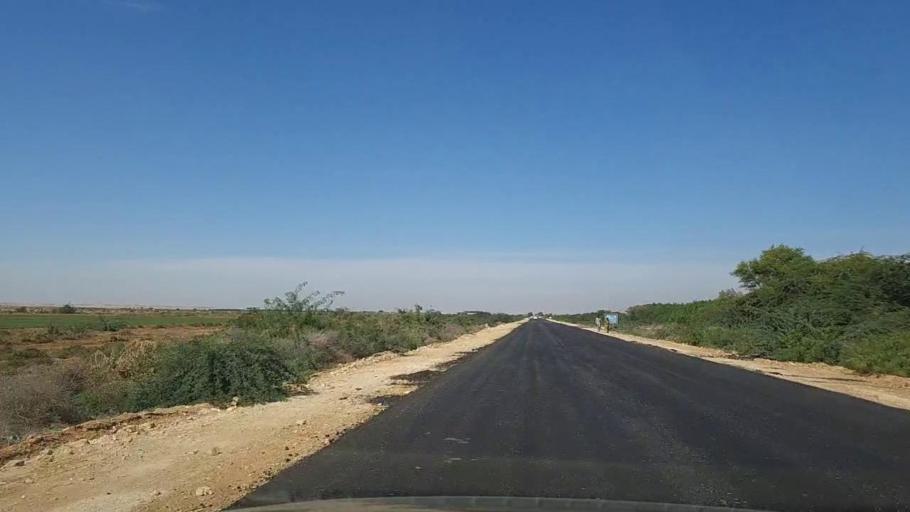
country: PK
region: Sindh
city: Kotri
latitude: 25.2358
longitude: 68.2329
